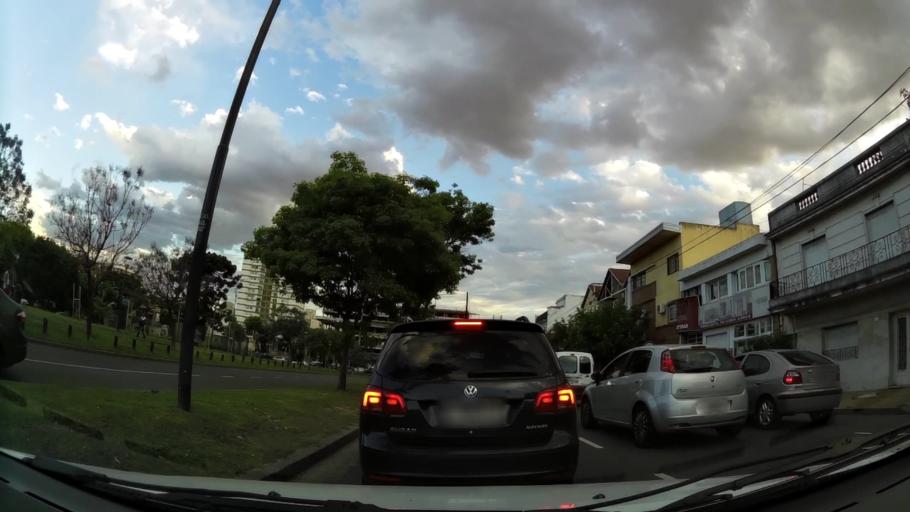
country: AR
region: Buenos Aires F.D.
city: Colegiales
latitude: -34.5644
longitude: -58.4820
